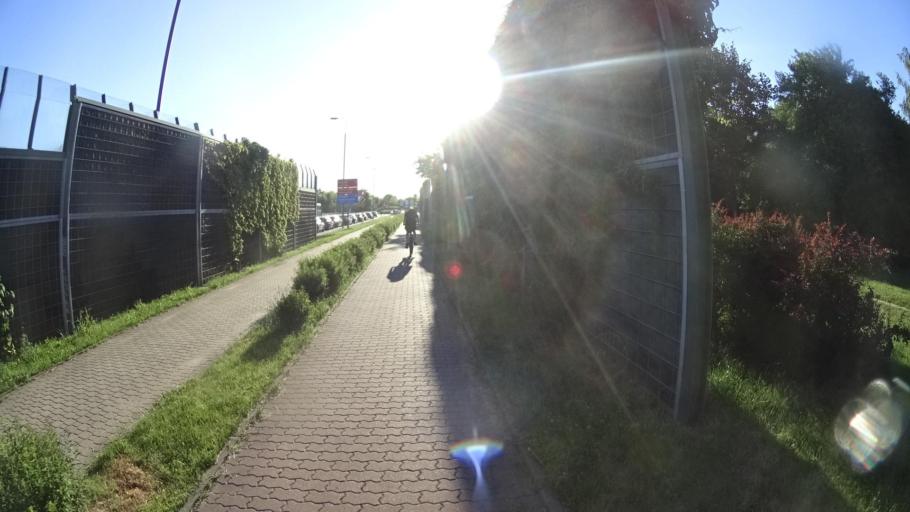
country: PL
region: Masovian Voivodeship
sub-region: Warszawa
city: Bielany
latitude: 52.2684
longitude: 20.9348
